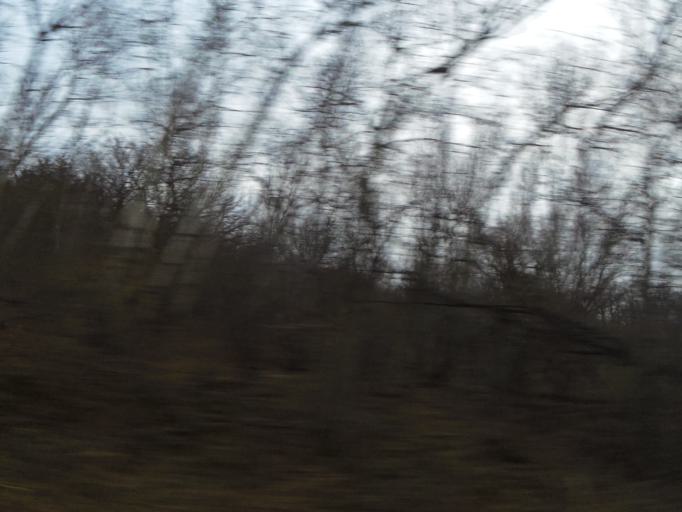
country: US
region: Wisconsin
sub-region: Pierce County
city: River Falls
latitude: 44.8795
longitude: -92.6064
